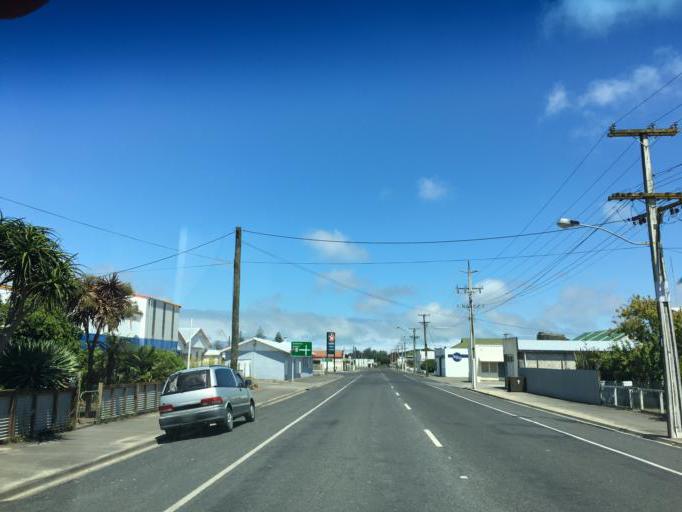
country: NZ
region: Hawke's Bay
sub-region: Wairoa District
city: Wairoa
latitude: -39.0260
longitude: 177.4175
